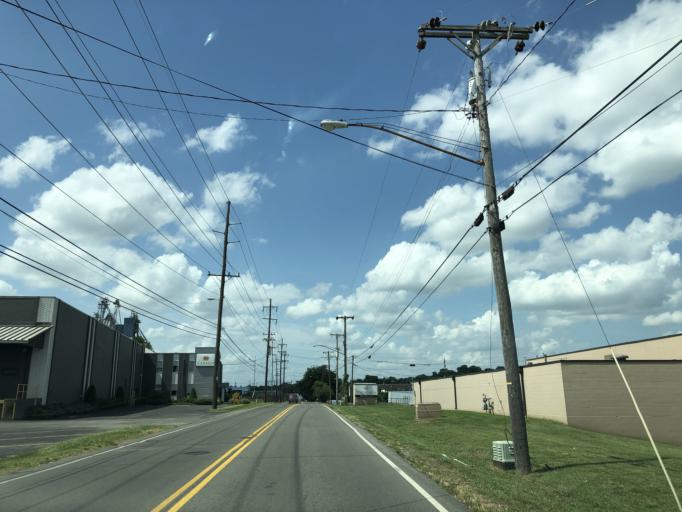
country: US
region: Tennessee
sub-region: Davidson County
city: Oak Hill
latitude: 36.0937
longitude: -86.7498
